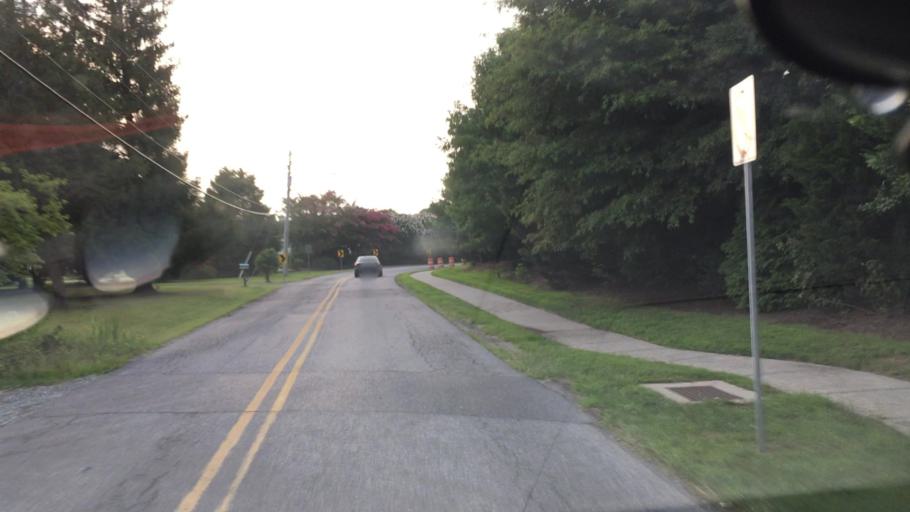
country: US
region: Delaware
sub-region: Sussex County
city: Ocean View
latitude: 38.5389
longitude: -75.0943
